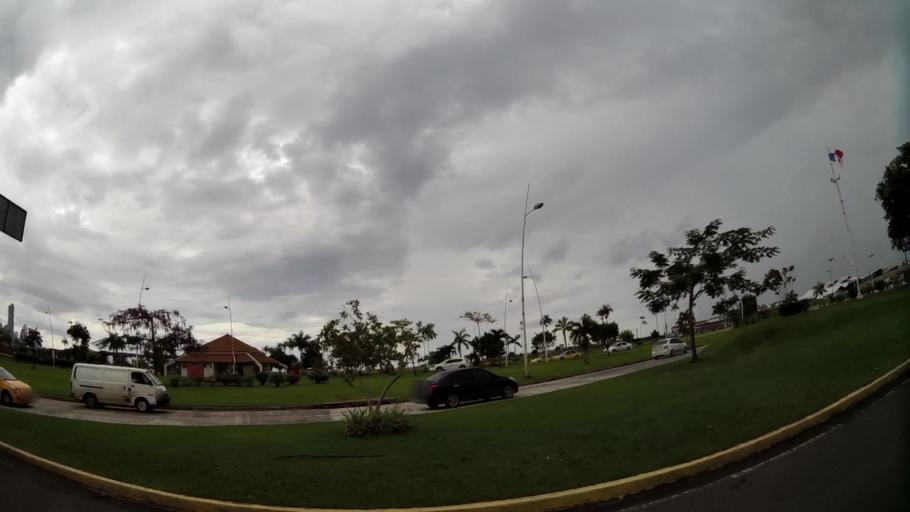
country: PA
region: Panama
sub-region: Distrito de Panama
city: Ancon
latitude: 8.9610
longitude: -79.5367
